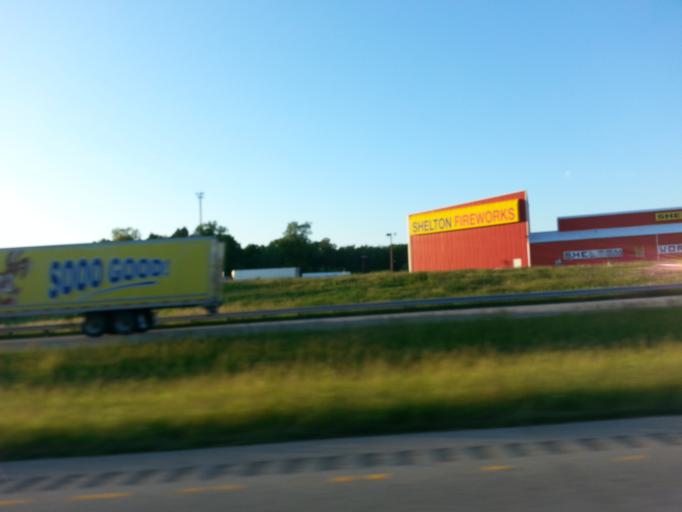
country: US
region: Indiana
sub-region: Fountain County
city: Covington
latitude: 40.1218
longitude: -87.3798
